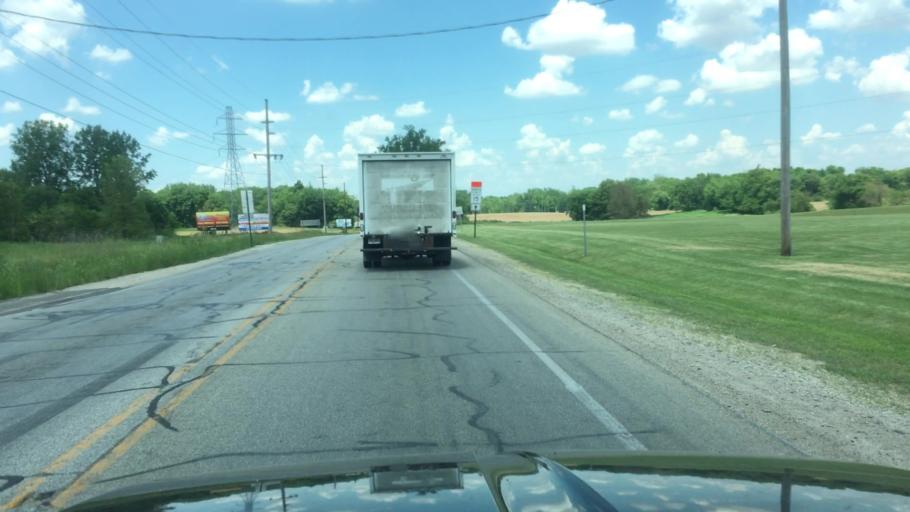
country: US
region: Indiana
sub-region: Kosciusko County
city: North Webster
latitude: 41.3092
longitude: -85.6910
